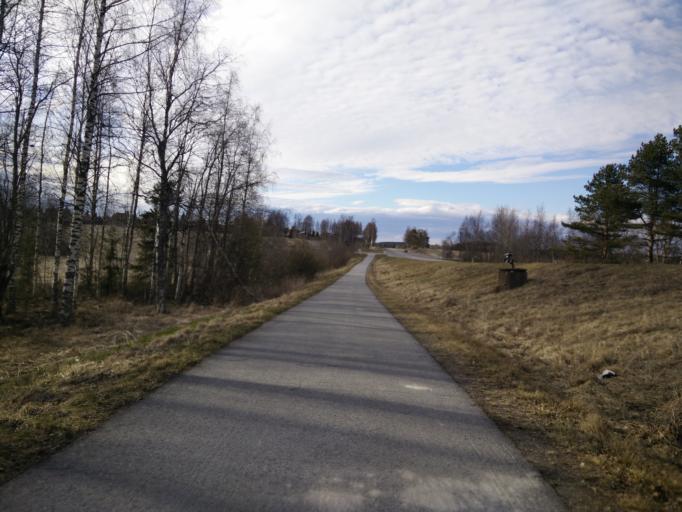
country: FI
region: Pirkanmaa
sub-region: Tampere
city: Orivesi
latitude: 61.7066
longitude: 24.3355
